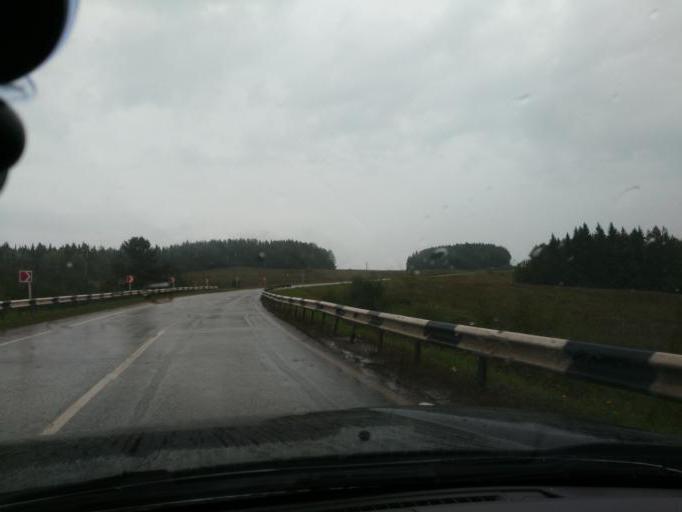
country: RU
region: Perm
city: Osa
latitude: 57.3089
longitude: 55.6198
